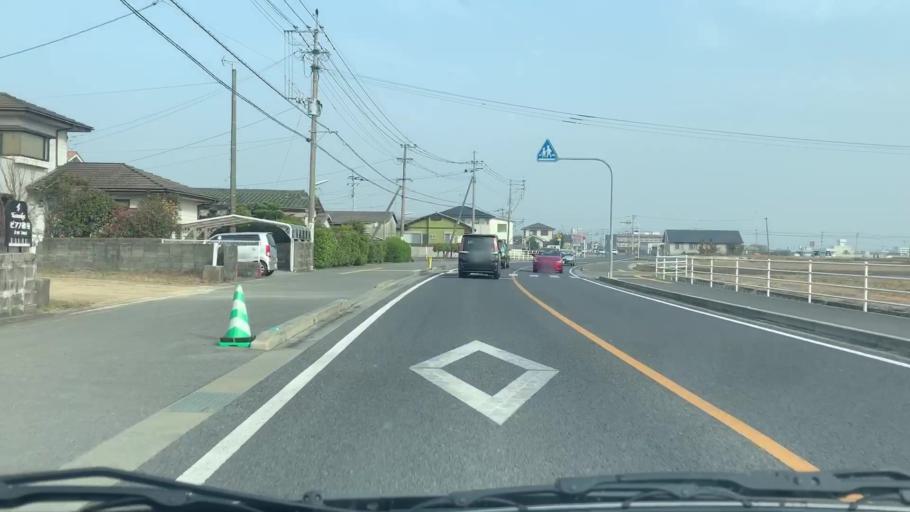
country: JP
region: Saga Prefecture
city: Saga-shi
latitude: 33.2345
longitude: 130.2575
